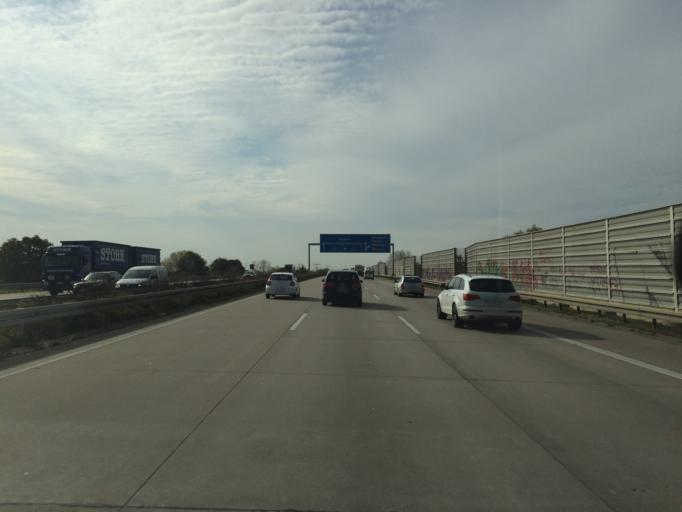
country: DE
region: Saxony-Anhalt
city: Barleben
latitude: 52.1945
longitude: 11.6354
